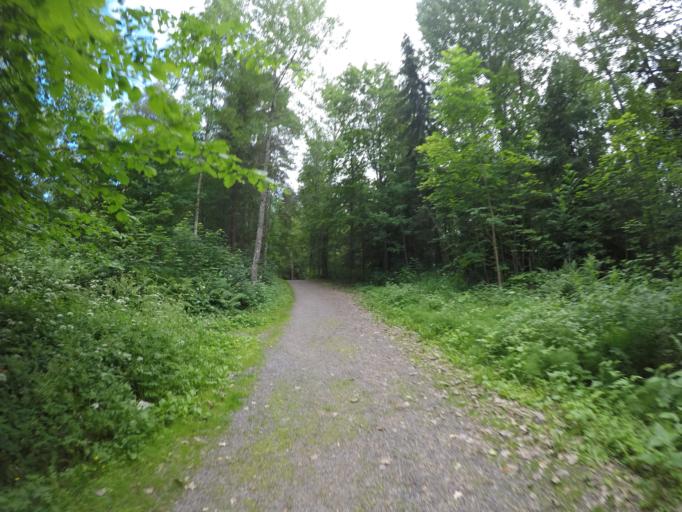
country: FI
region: Haeme
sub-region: Haemeenlinna
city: Haemeenlinna
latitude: 61.0111
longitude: 24.4472
